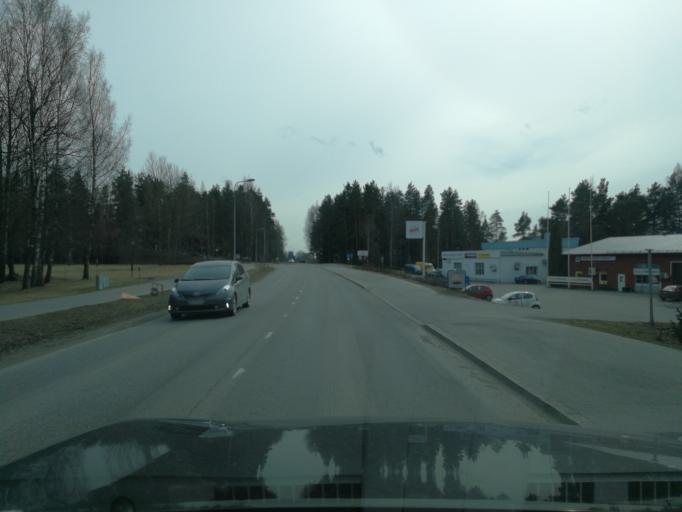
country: FI
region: Uusimaa
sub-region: Helsinki
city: Lohja
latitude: 60.1867
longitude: 23.9959
